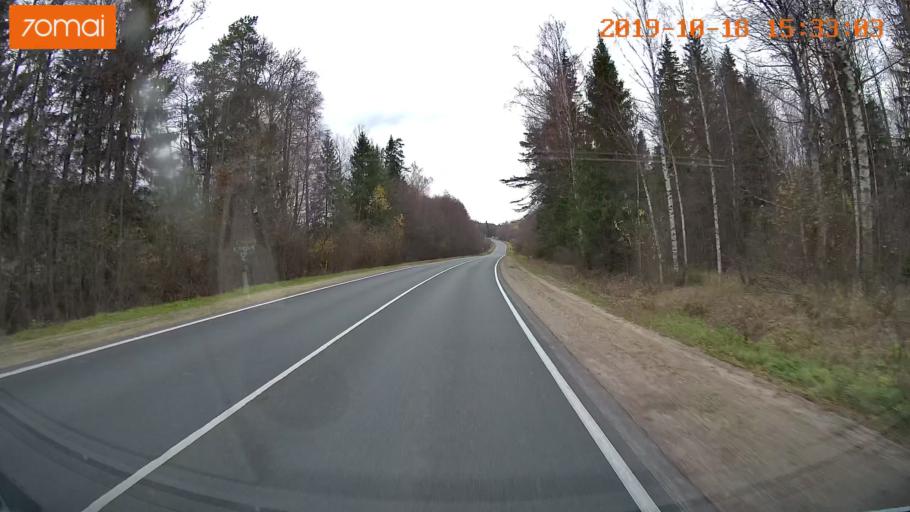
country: RU
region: Vladimir
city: Anopino
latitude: 55.8343
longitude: 40.6438
